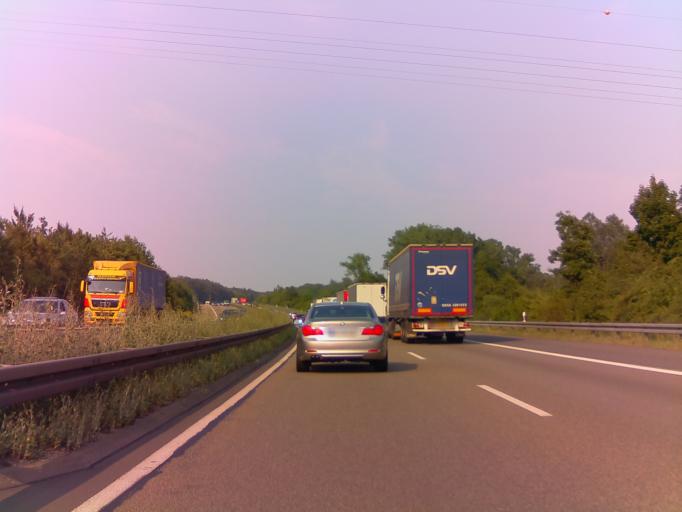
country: DE
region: Hesse
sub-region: Regierungsbezirk Giessen
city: Homberg
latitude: 50.7086
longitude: 9.0631
